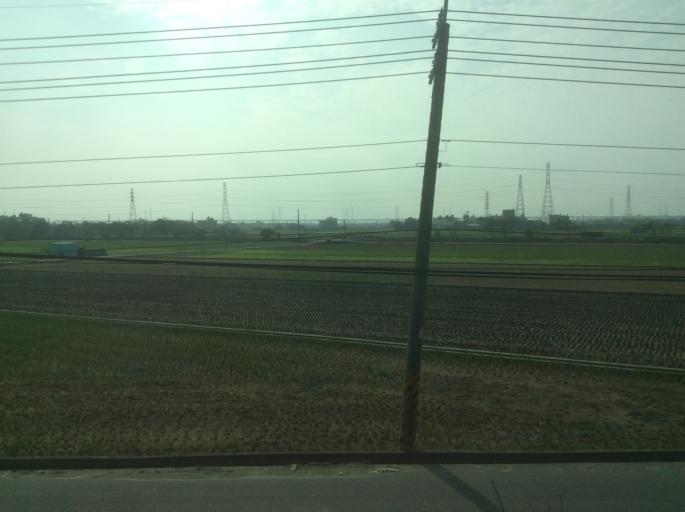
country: TW
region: Taiwan
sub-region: Changhua
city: Chang-hua
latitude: 24.1370
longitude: 120.5494
